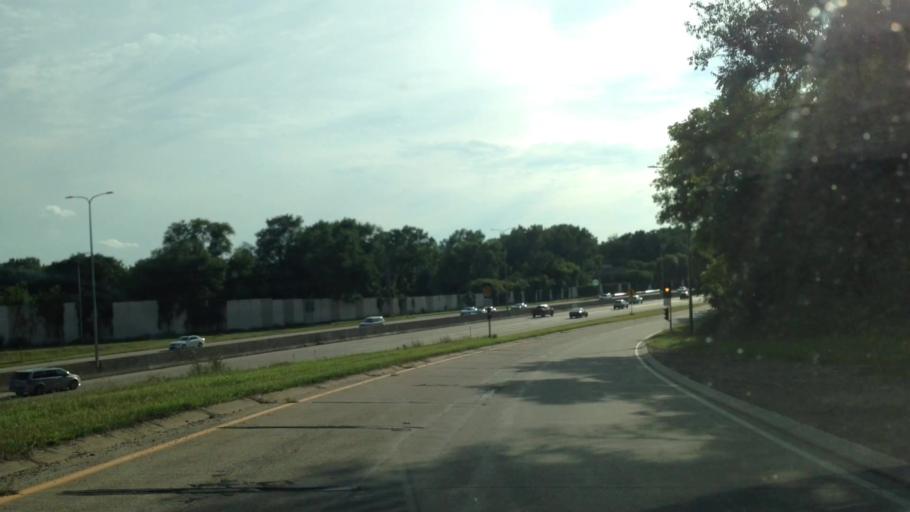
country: US
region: Minnesota
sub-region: Ramsey County
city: New Brighton
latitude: 45.0657
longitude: -93.2033
